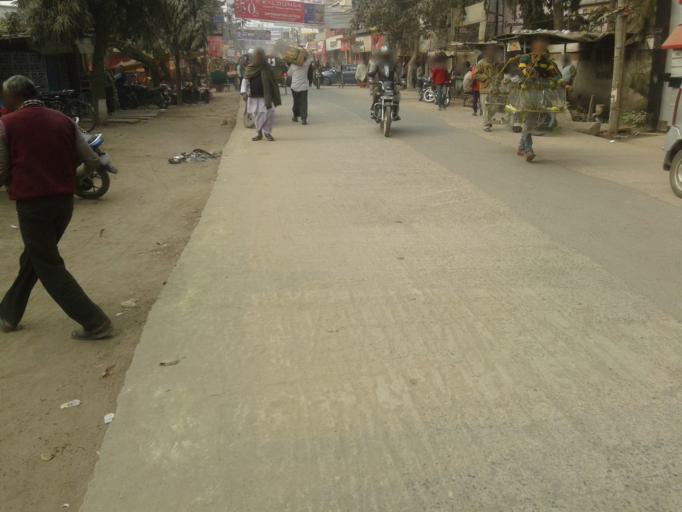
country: IN
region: Bihar
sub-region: Muzaffarpur
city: Muzaffarpur
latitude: 26.1151
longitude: 85.3955
